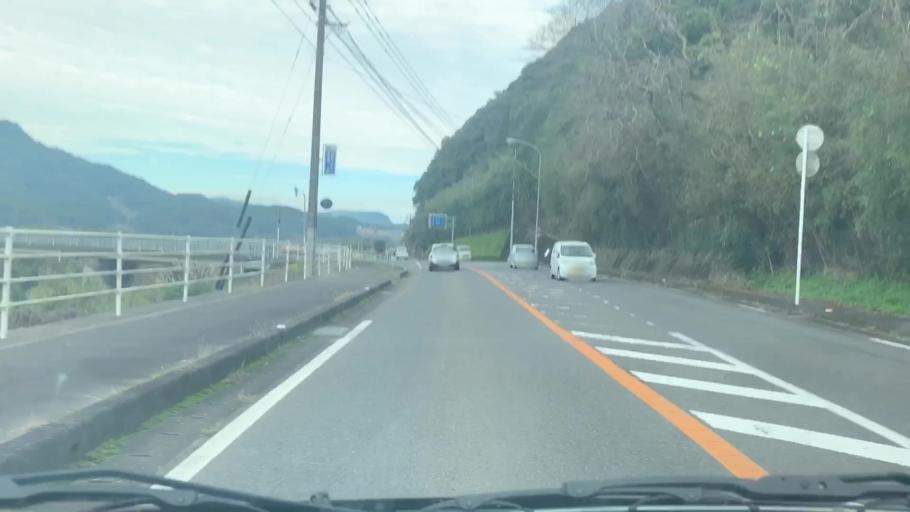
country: JP
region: Saga Prefecture
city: Imaricho-ko
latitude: 33.2706
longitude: 129.9646
